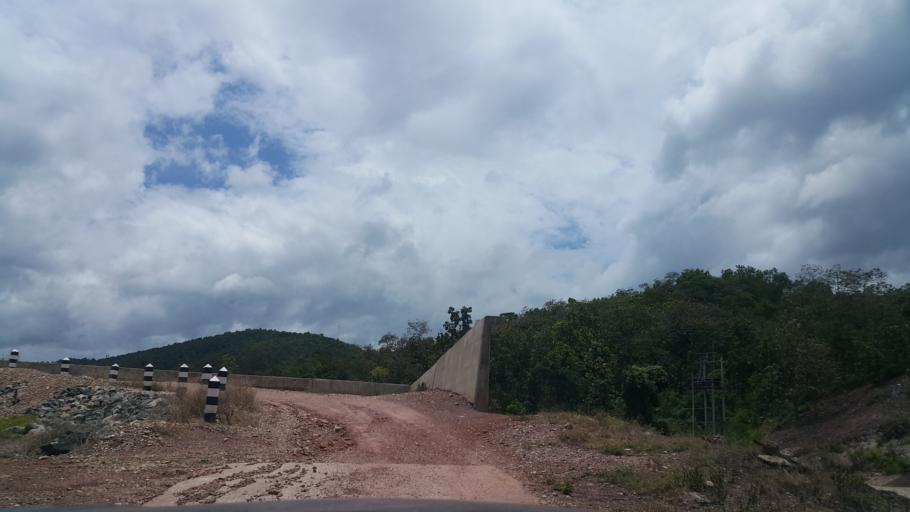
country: TH
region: Chiang Mai
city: Mae Taeng
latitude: 19.2263
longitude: 99.0108
